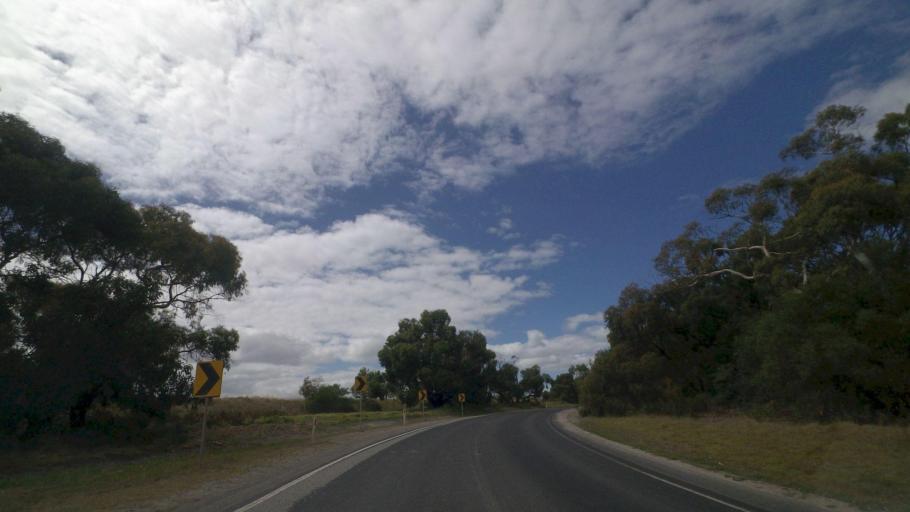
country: AU
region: Victoria
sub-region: Cardinia
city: Koo-Wee-Rup
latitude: -38.2744
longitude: 145.5751
